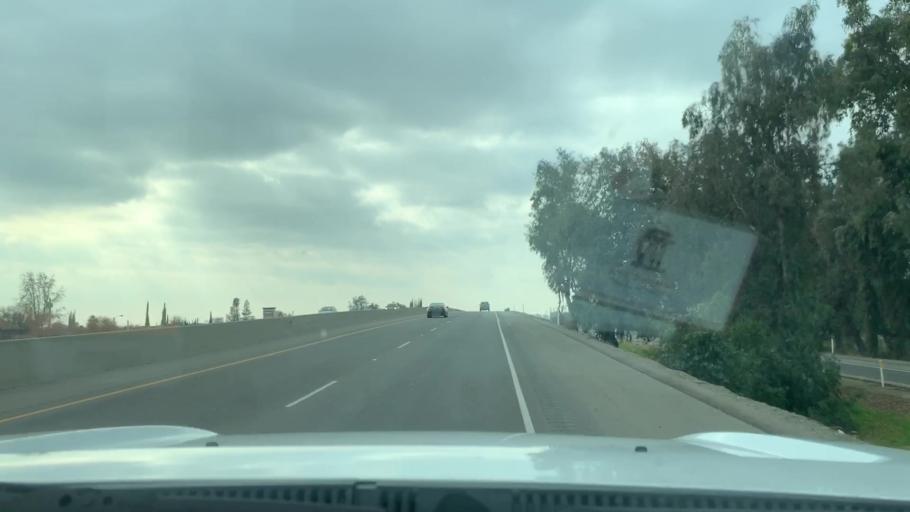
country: US
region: California
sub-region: Kings County
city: Armona
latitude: 36.3098
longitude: -119.7068
